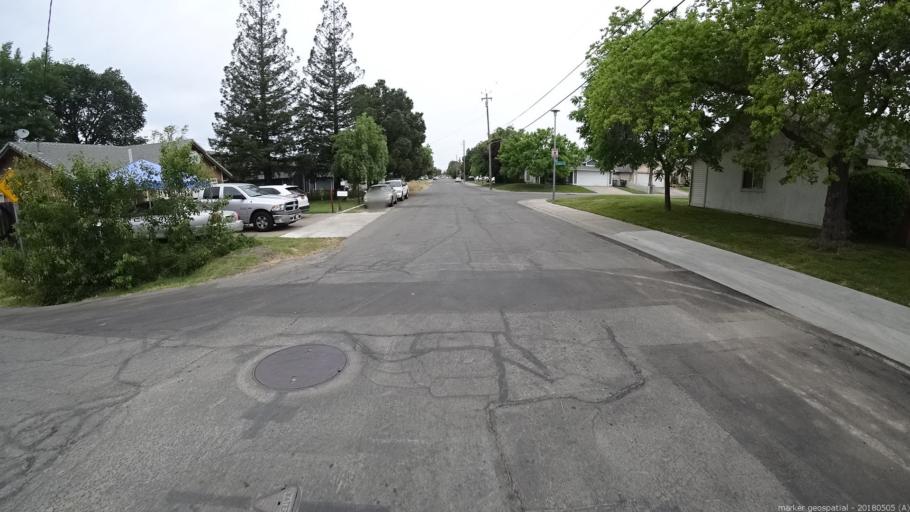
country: US
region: California
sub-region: Sacramento County
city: Rio Linda
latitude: 38.6448
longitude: -121.4431
